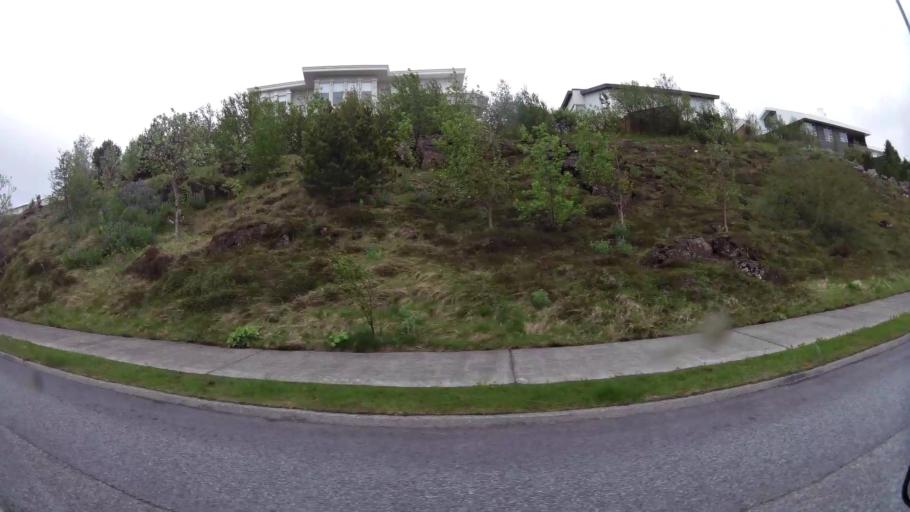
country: IS
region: Capital Region
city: Hafnarfjoerdur
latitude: 64.0609
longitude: -21.9245
